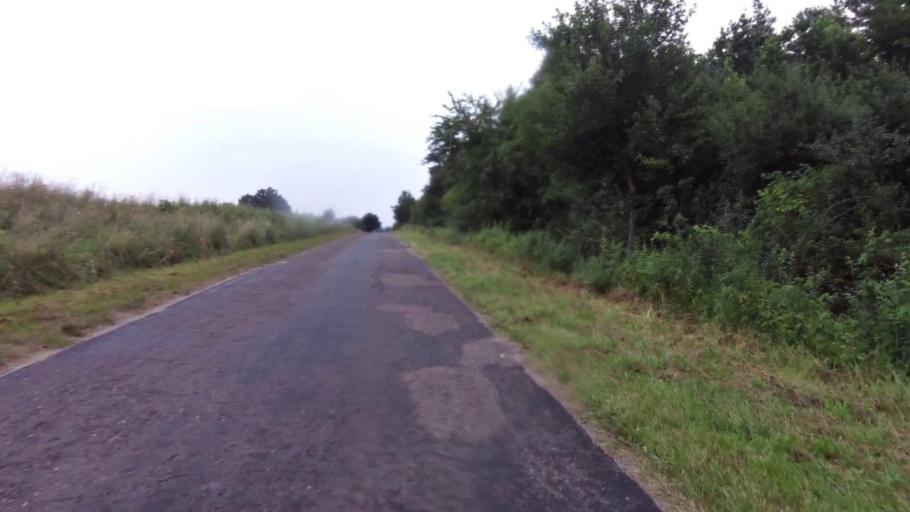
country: PL
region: West Pomeranian Voivodeship
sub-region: Powiat lobeski
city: Wegorzyno
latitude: 53.5335
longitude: 15.6594
